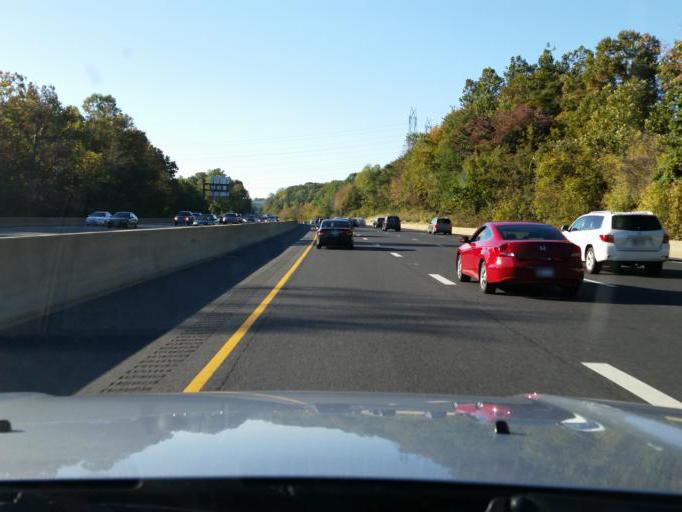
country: US
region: Maryland
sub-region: Montgomery County
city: Gaithersburg
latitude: 39.1576
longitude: -77.2270
